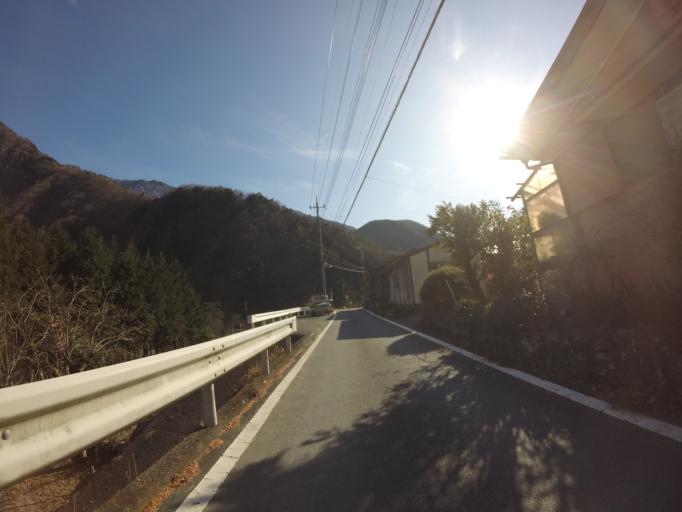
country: JP
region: Yamanashi
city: Ryuo
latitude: 35.3942
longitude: 138.3230
